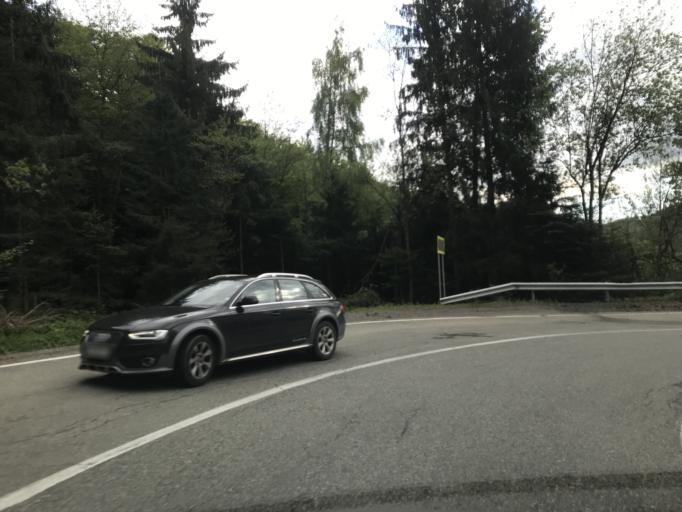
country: RO
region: Sibiu
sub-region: Comuna Cartisoara
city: Cartisoara
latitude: 45.6757
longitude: 24.5883
